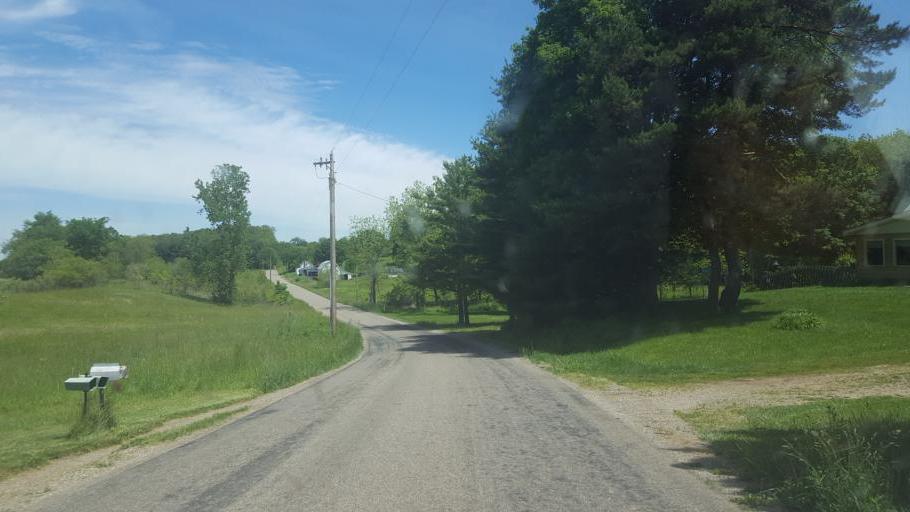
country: US
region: Ohio
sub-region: Knox County
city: Oak Hill
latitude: 40.3701
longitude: -82.3106
